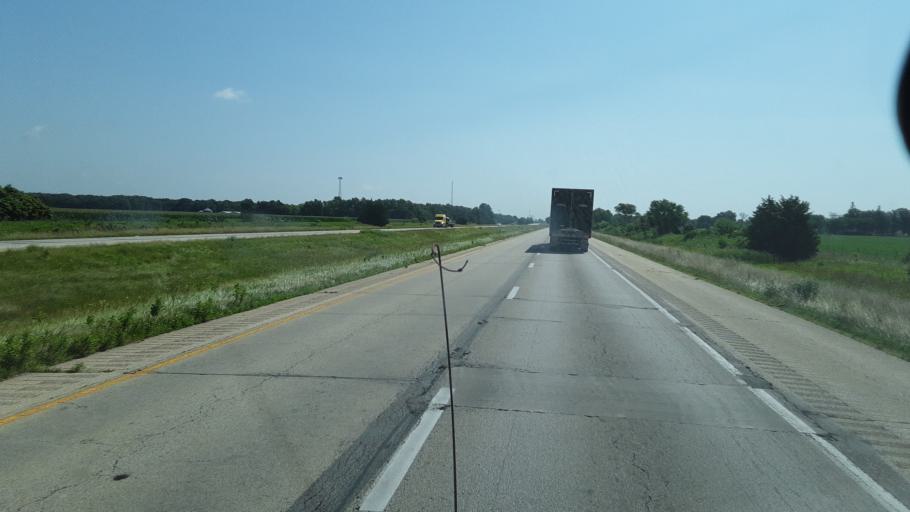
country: US
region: Illinois
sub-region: Effingham County
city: Teutopolis
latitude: 39.1671
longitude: -88.3919
